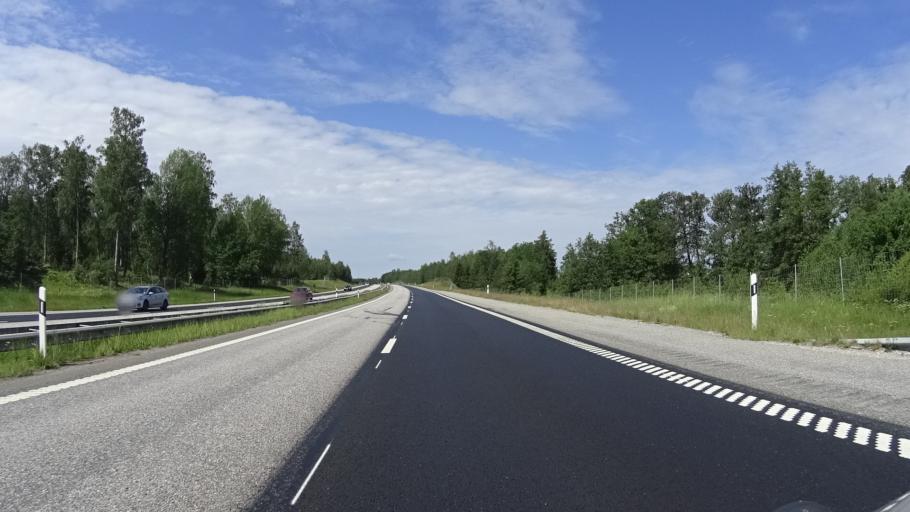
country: SE
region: Soedermanland
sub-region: Strangnas Kommun
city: Strangnas
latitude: 59.3649
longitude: 16.8698
